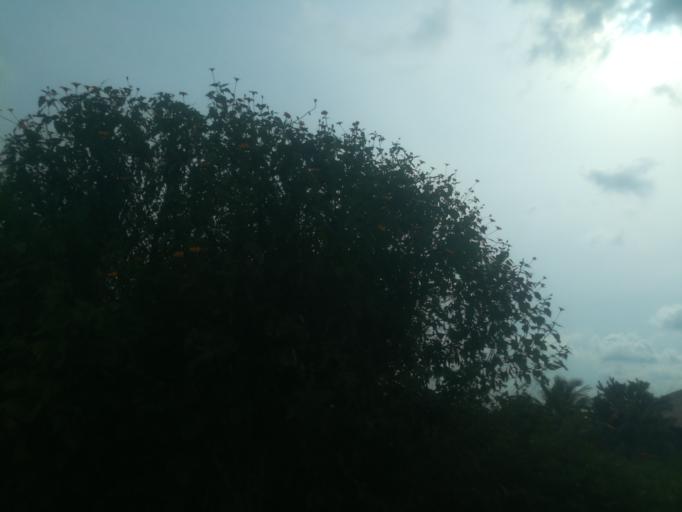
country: NG
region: Ogun
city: Ayetoro
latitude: 7.3898
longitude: 3.0180
